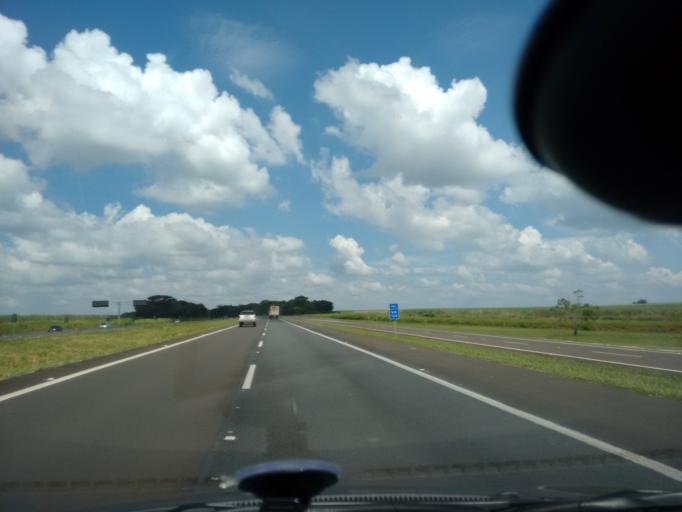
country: BR
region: Sao Paulo
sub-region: Santa Barbara D'Oeste
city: Santa Barbara d'Oeste
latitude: -22.7671
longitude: -47.4458
